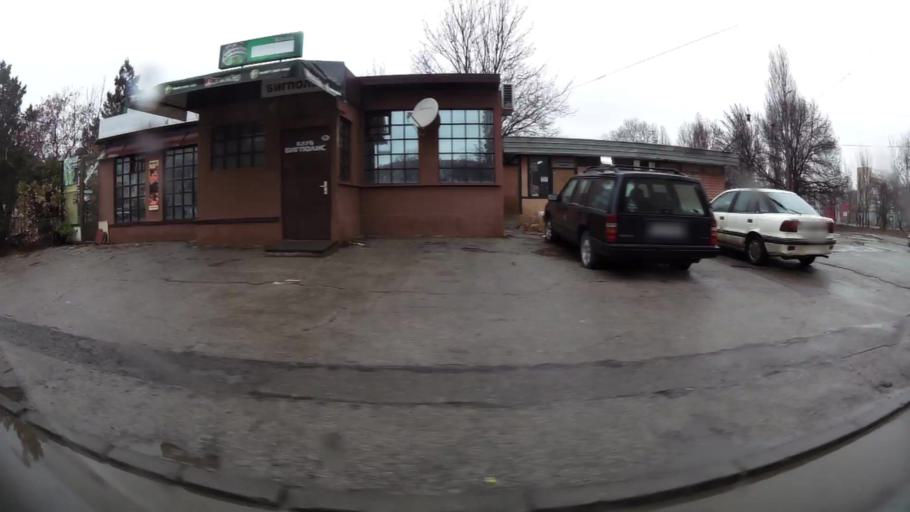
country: BG
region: Sofia-Capital
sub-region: Stolichna Obshtina
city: Sofia
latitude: 42.6663
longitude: 23.3974
